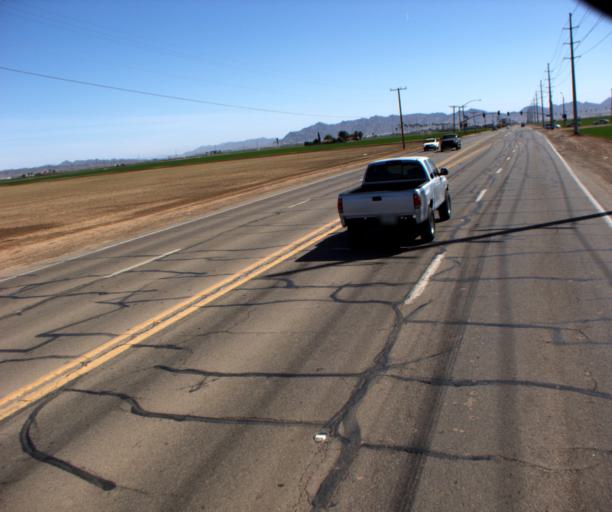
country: US
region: Arizona
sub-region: Yuma County
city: Yuma
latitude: 32.6991
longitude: -114.5238
